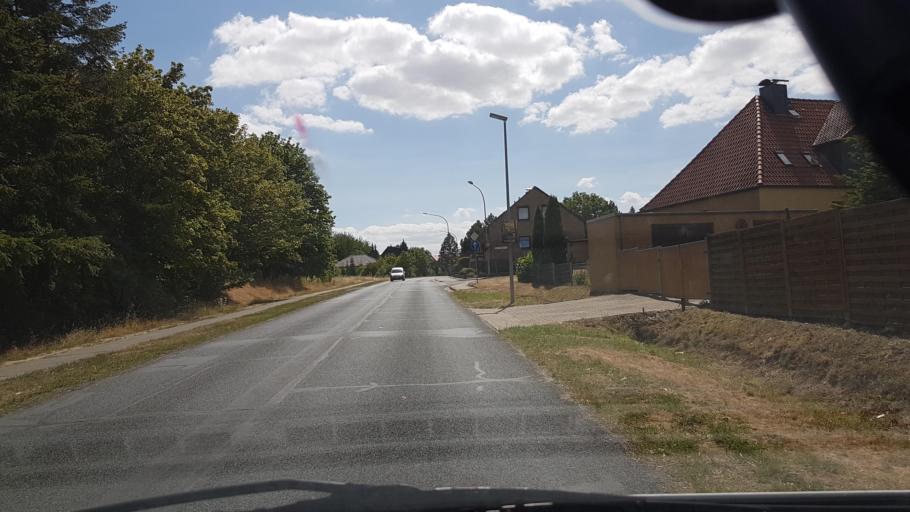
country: DE
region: Lower Saxony
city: Schoningen
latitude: 52.1452
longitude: 10.9753
